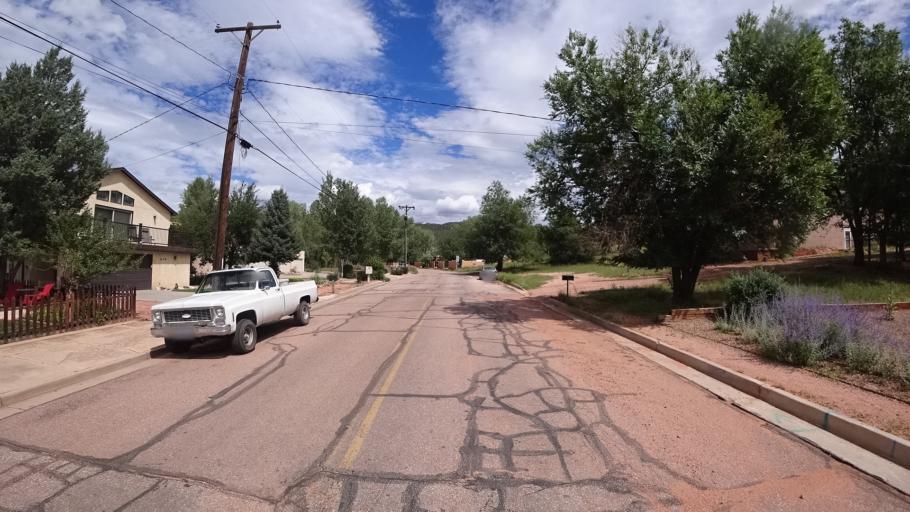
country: US
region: Colorado
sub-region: El Paso County
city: Manitou Springs
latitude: 38.8620
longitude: -104.8922
